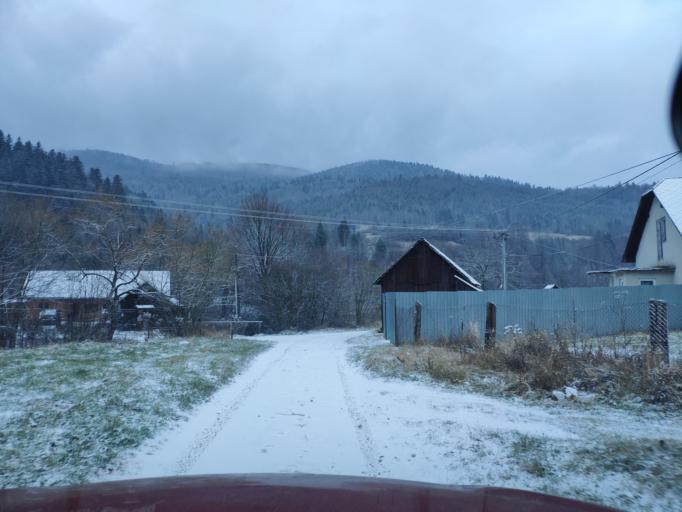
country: SK
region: Kosicky
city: Spisska Nova Ves
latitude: 48.8168
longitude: 20.5739
